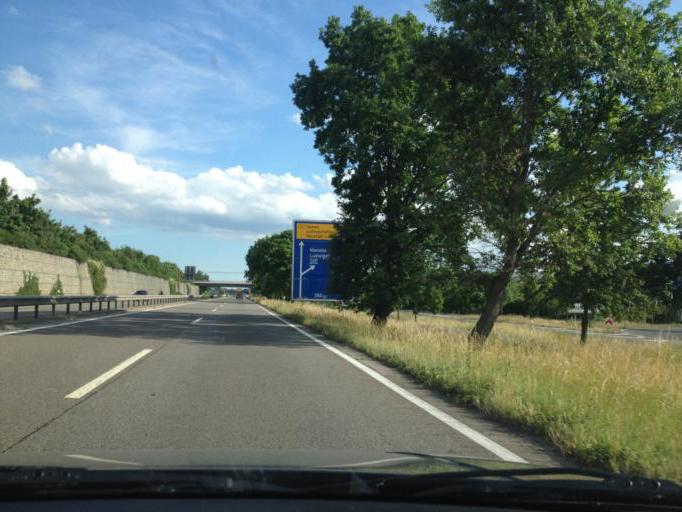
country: DE
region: Rheinland-Pfalz
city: Mutterstadt
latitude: 49.4873
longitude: 8.3577
